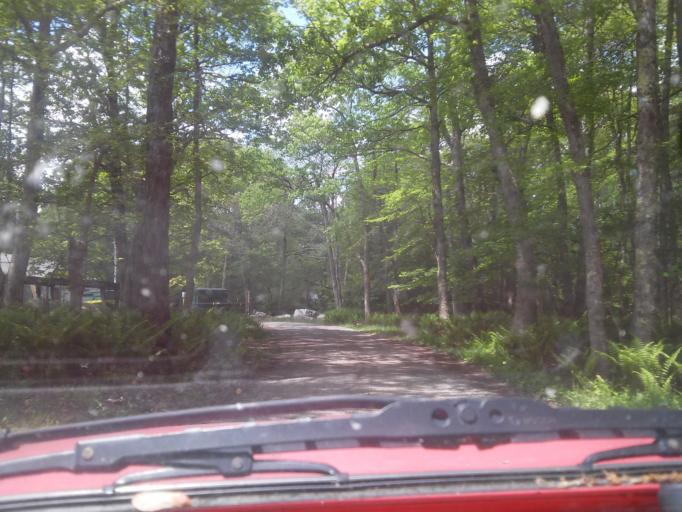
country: US
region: Virginia
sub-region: Giles County
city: Pembroke
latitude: 37.3764
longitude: -80.5234
